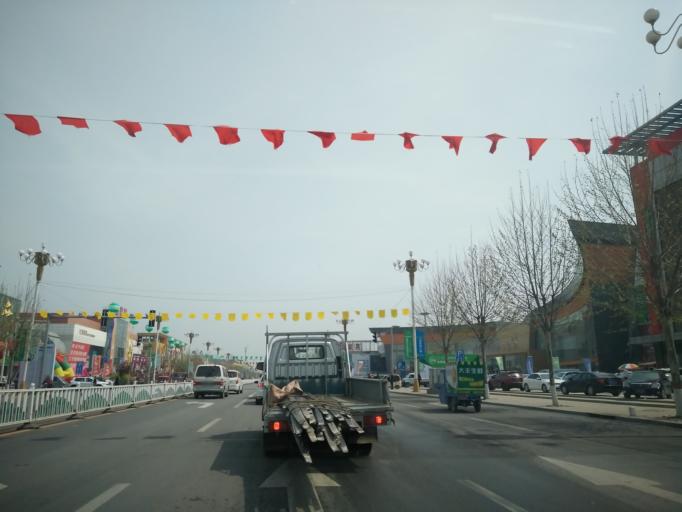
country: CN
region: Tianjin Shi
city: Xiawuqi
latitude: 39.7491
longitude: 117.0122
